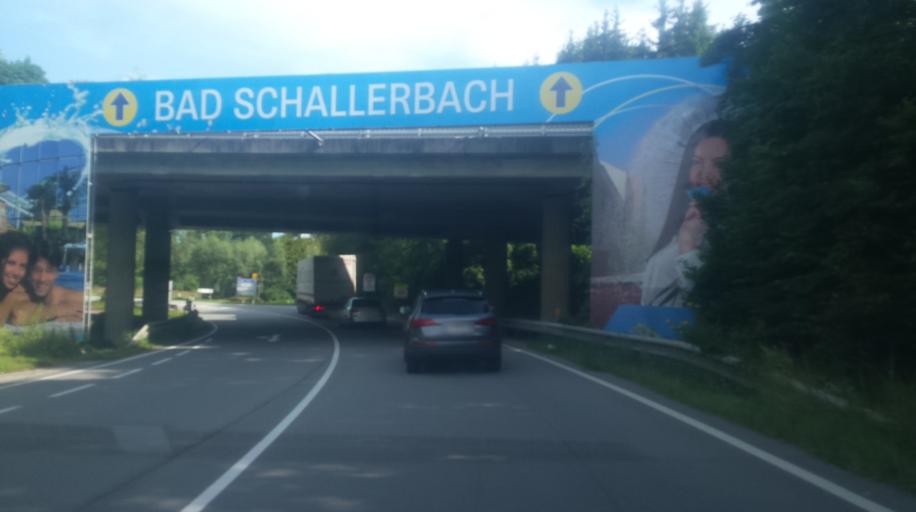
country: AT
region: Upper Austria
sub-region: Politischer Bezirk Grieskirchen
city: Bad Schallerbach
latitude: 48.2219
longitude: 13.9358
